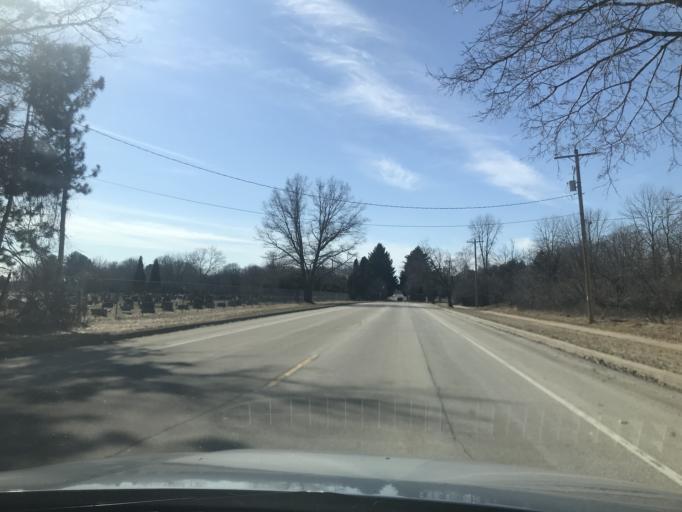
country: US
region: Wisconsin
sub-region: Marinette County
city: Marinette
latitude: 45.1119
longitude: -87.6489
